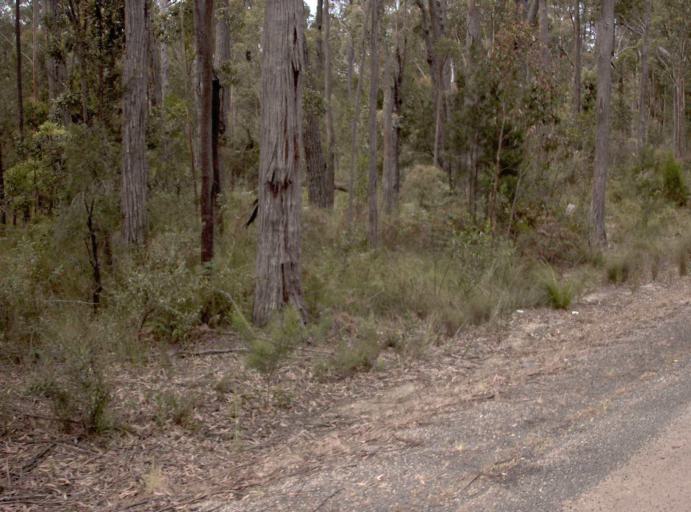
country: AU
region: New South Wales
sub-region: Bega Valley
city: Eden
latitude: -37.5078
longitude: 149.5260
